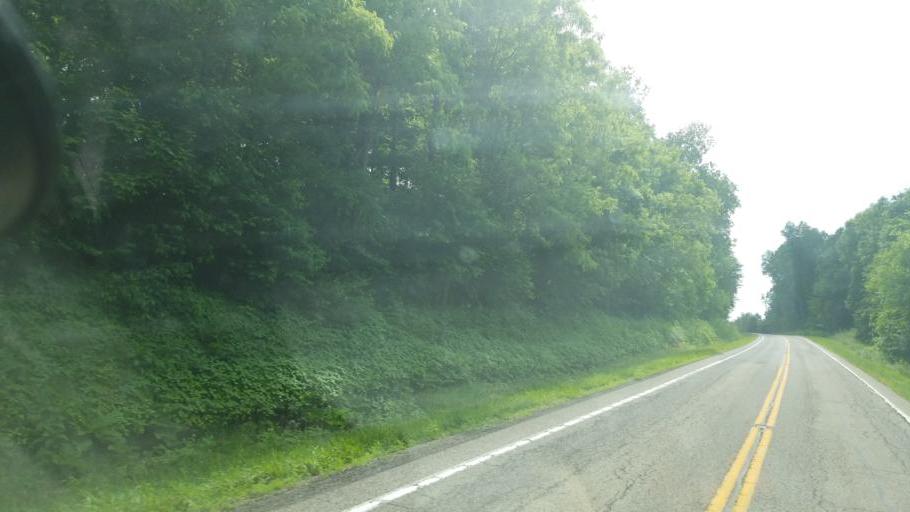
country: US
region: Ohio
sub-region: Knox County
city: Oak Hill
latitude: 40.2902
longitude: -82.1945
